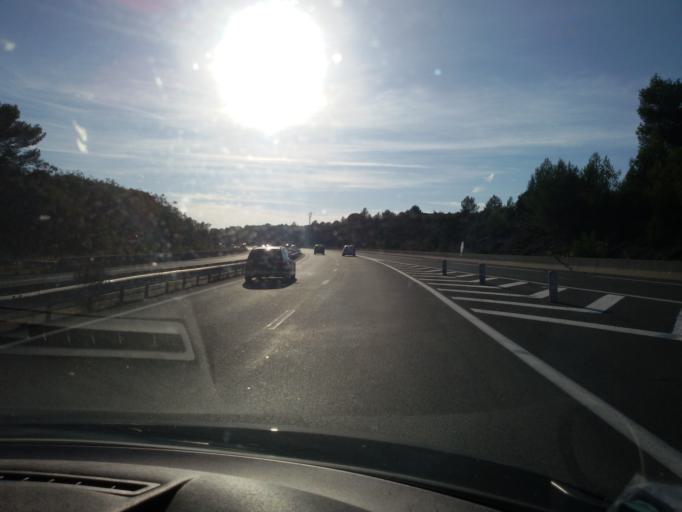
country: FR
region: Languedoc-Roussillon
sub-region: Departement de l'Herault
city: Murviel-les-Montpellier
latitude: 43.6340
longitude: 3.7553
